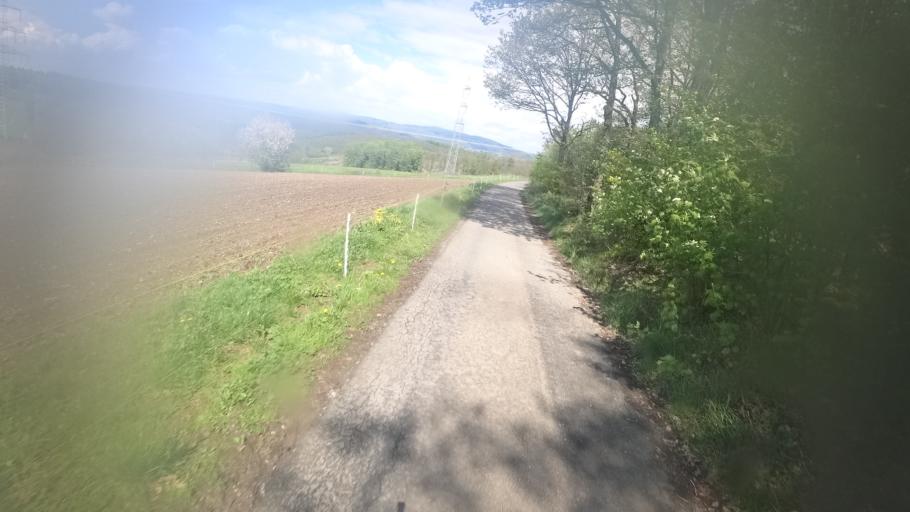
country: DE
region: Rheinland-Pfalz
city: Alsdorf
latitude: 50.7713
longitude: 7.8499
